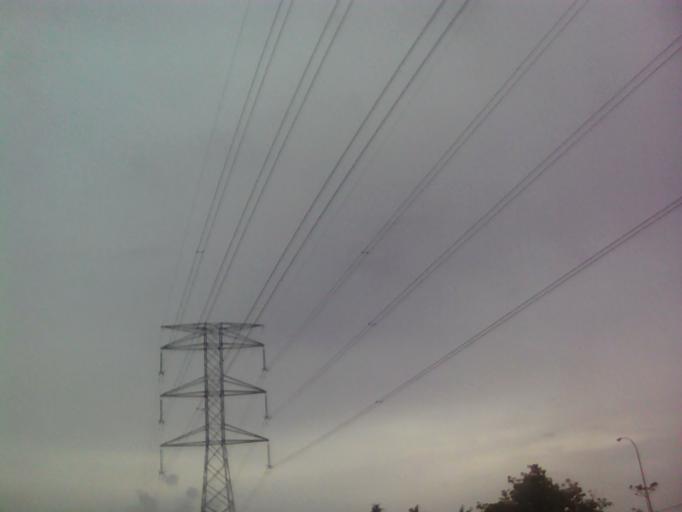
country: MY
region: Penang
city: Perai
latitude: 5.3989
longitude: 100.4105
